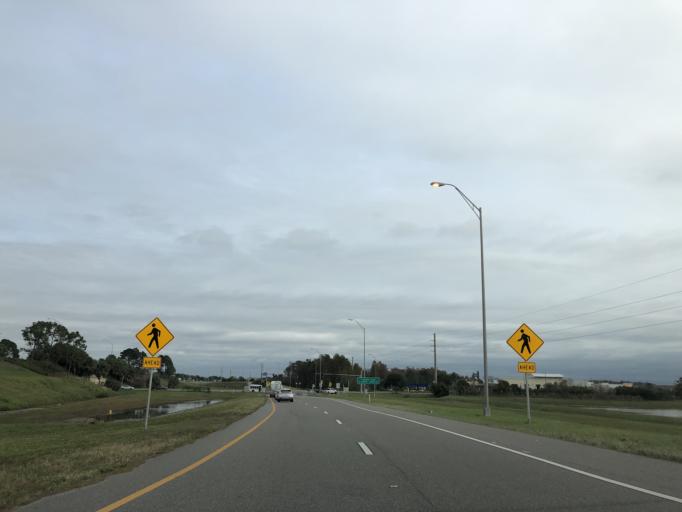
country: US
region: Florida
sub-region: Orange County
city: Meadow Woods
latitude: 28.3679
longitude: -81.3691
